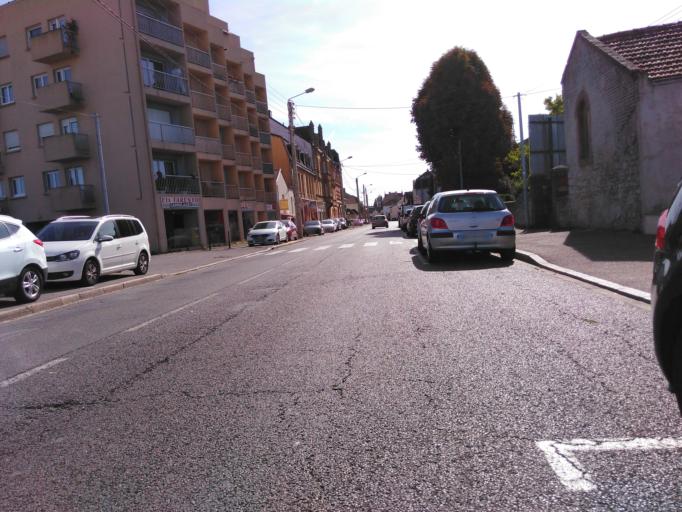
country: FR
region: Lorraine
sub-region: Departement de la Moselle
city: Thionville
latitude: 49.3707
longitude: 6.1692
